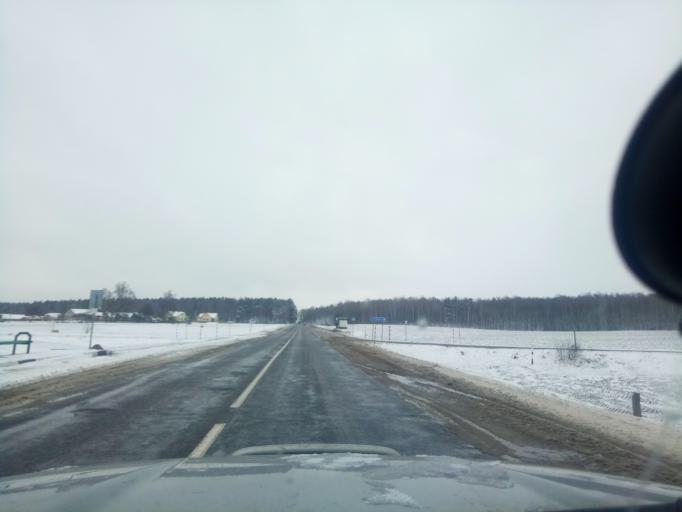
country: BY
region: Minsk
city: Kapyl'
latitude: 53.1232
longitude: 27.0735
